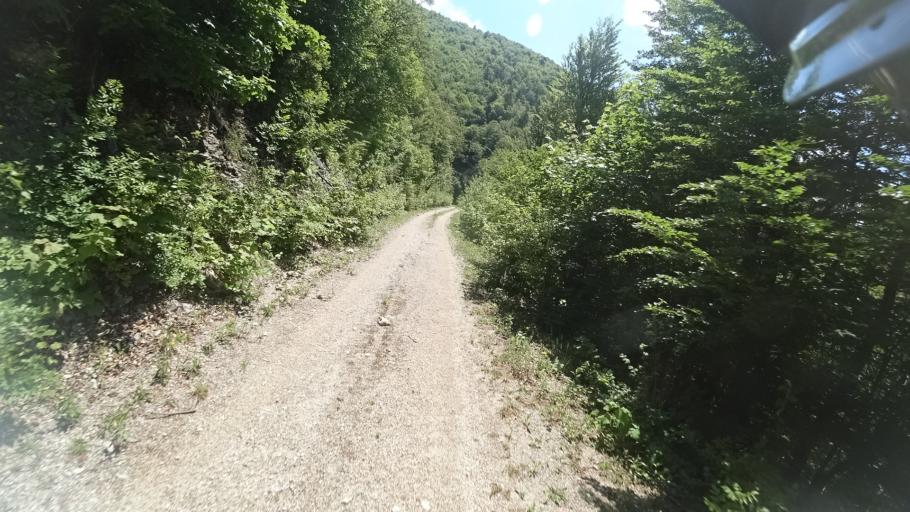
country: BA
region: Federation of Bosnia and Herzegovina
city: Orasac
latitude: 44.5702
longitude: 15.8533
